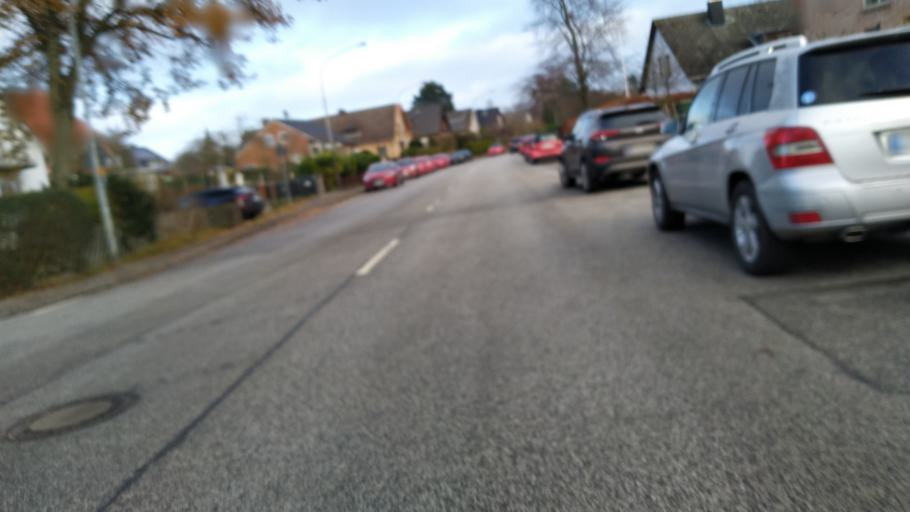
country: DE
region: Schleswig-Holstein
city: Travemuende
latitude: 53.9645
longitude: 10.8669
